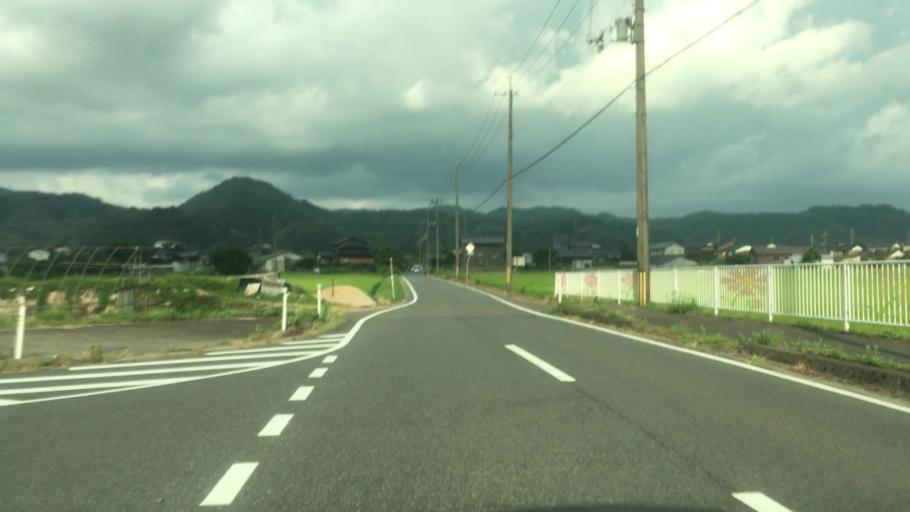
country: JP
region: Hyogo
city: Toyooka
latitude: 35.5647
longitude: 134.8080
